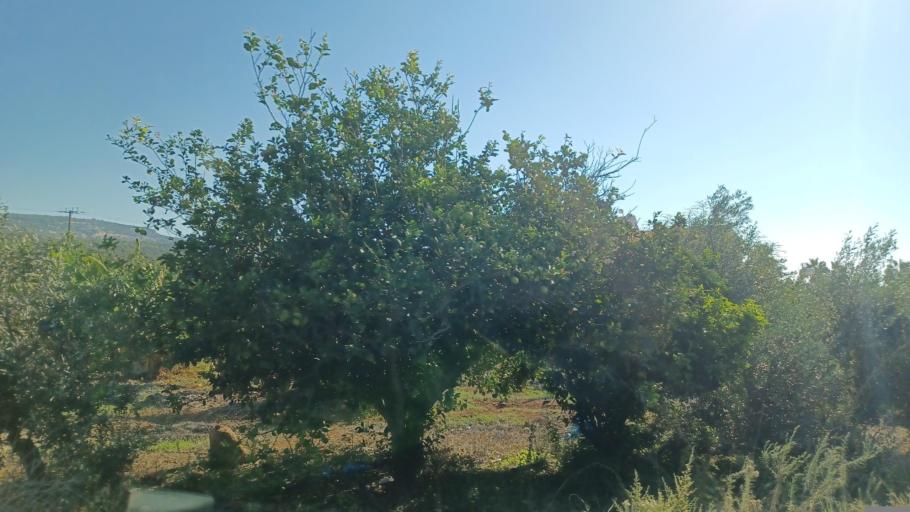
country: CY
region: Pafos
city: Pegeia
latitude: 34.8911
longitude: 32.3351
